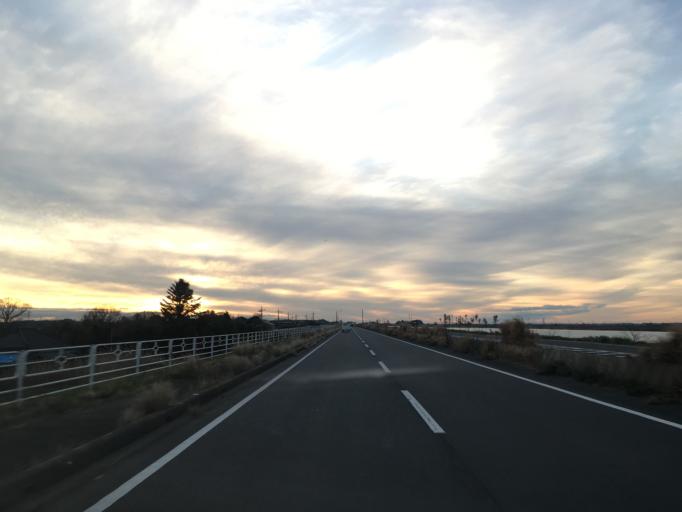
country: JP
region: Chiba
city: Katori-shi
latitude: 35.9135
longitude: 140.4495
